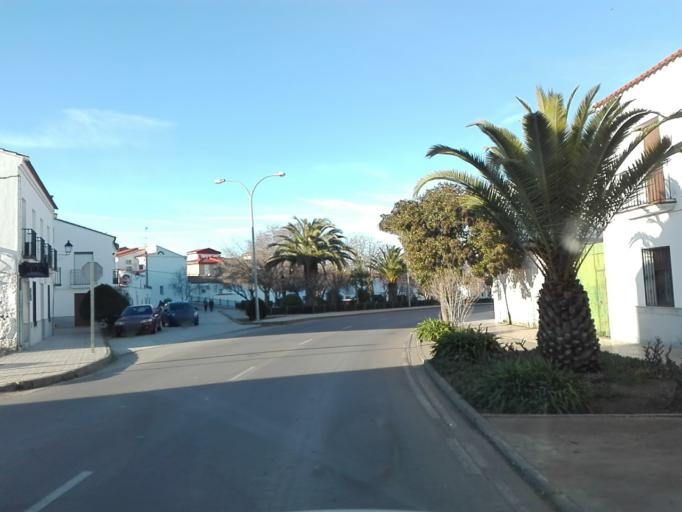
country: ES
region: Extremadura
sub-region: Provincia de Badajoz
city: Llerena
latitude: 38.2384
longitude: -6.0207
